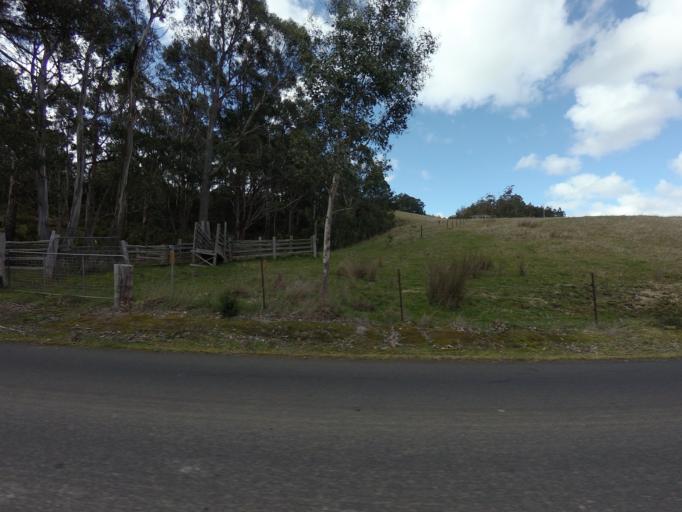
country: AU
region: Tasmania
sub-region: Huon Valley
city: Geeveston
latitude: -43.1898
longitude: 146.9360
